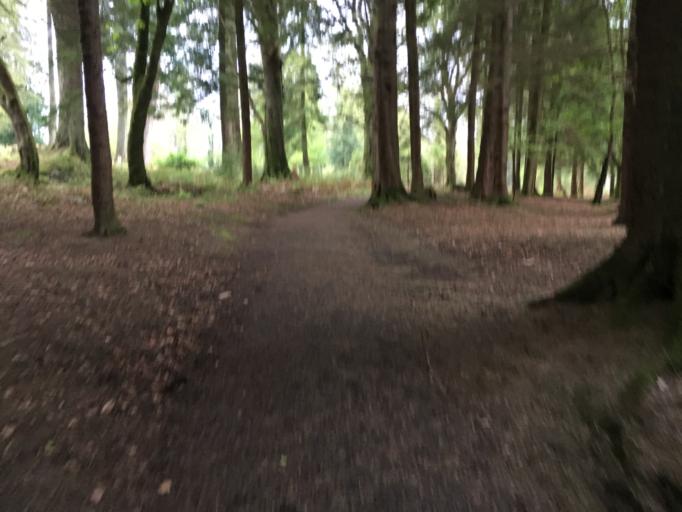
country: GB
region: Scotland
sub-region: Argyll and Bute
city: Rothesay
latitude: 55.7979
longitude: -5.0198
